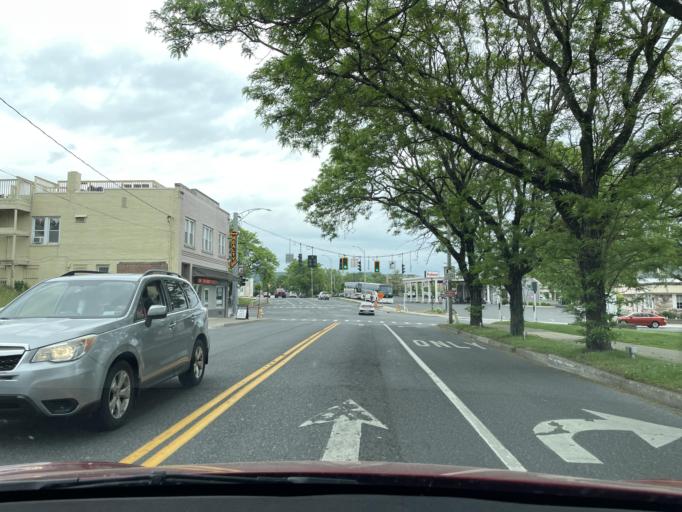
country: US
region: New York
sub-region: Ulster County
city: Kingston
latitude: 41.9345
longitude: -74.0247
